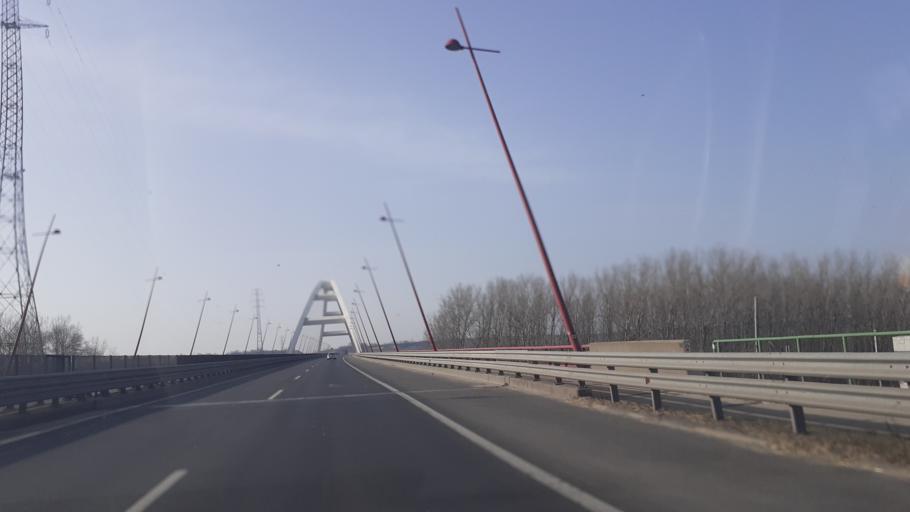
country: HU
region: Bacs-Kiskun
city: Dunavecse
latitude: 46.9016
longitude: 18.9638
